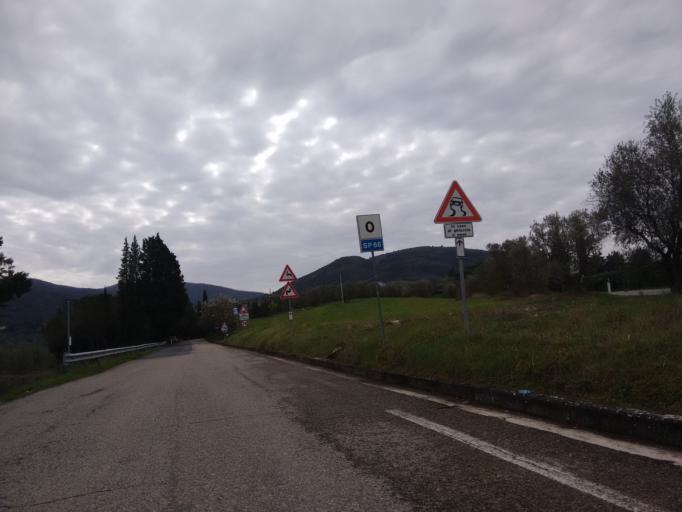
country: IT
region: Tuscany
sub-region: Province of Florence
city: Strada in Chianti
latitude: 43.6509
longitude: 11.3096
